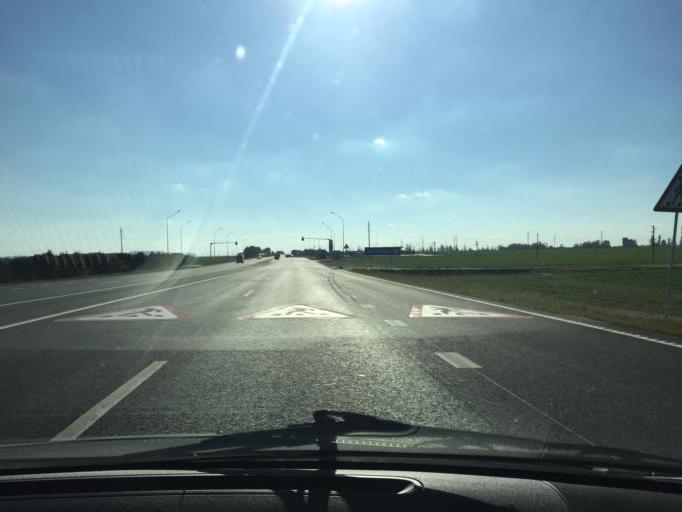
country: BY
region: Minsk
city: Slutsk
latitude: 52.9885
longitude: 27.5064
